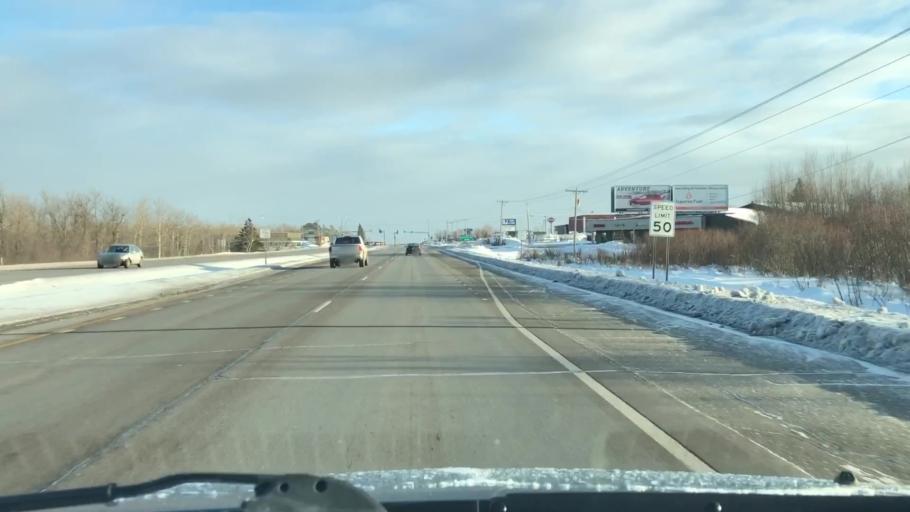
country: US
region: Minnesota
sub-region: Saint Louis County
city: Hermantown
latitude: 46.8299
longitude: -92.1996
